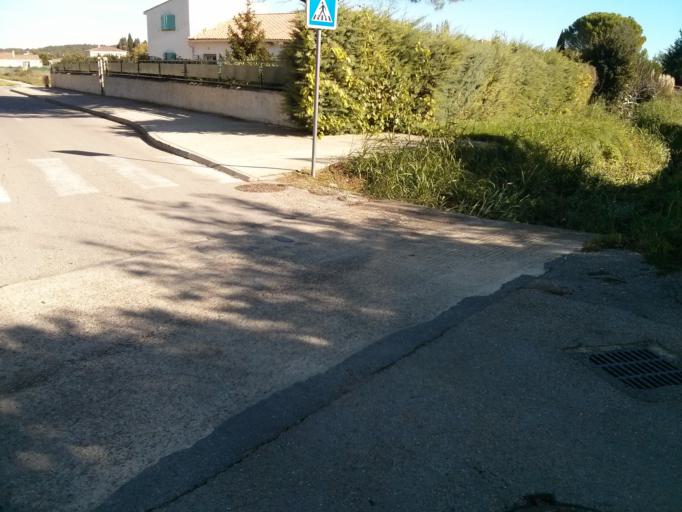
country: FR
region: Languedoc-Roussillon
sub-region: Departement du Gard
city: Aigues-Vives
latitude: 43.7421
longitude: 4.1811
